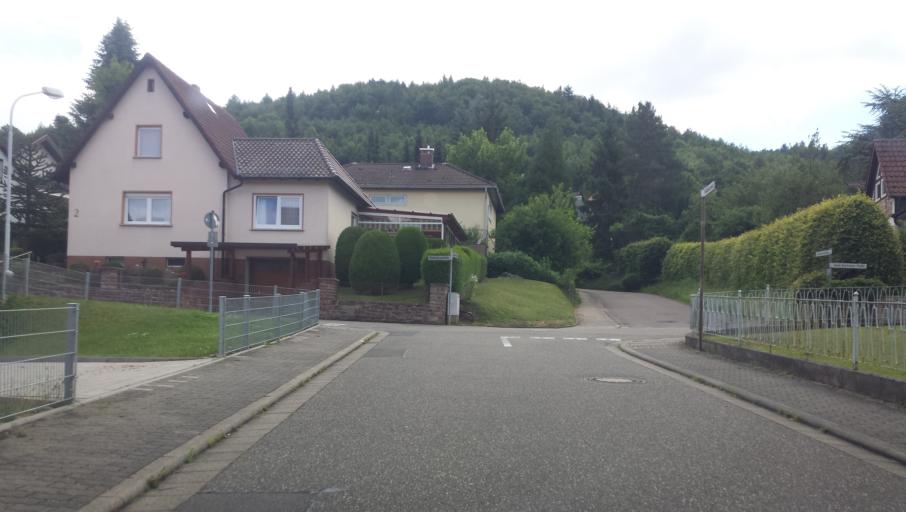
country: DE
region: Rheinland-Pfalz
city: Annweiler am Trifels
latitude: 49.2055
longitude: 7.9769
